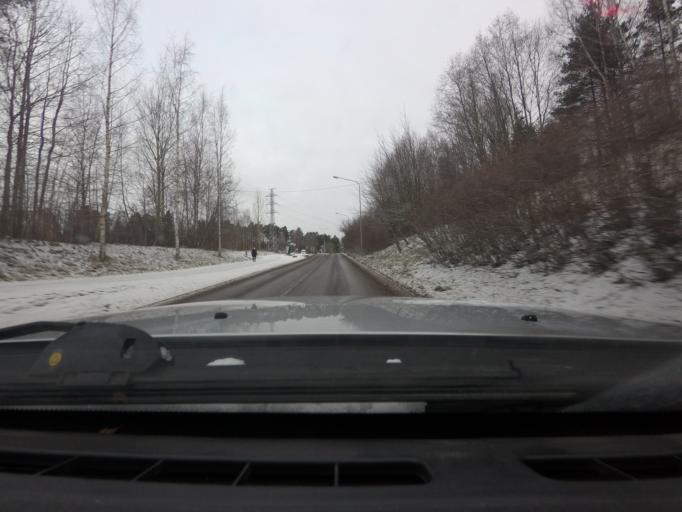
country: FI
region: Uusimaa
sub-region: Helsinki
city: Kilo
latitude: 60.2188
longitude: 24.7865
